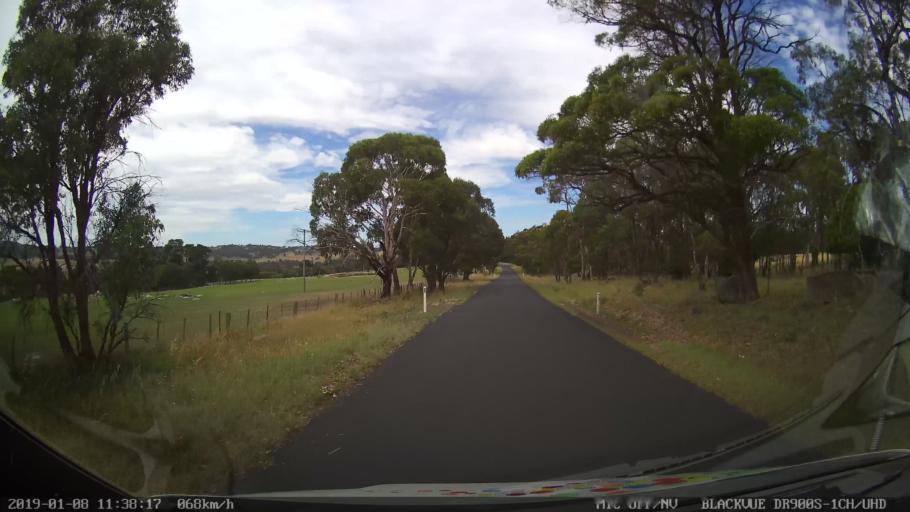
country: AU
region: New South Wales
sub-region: Guyra
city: Guyra
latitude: -30.3592
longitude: 151.5554
